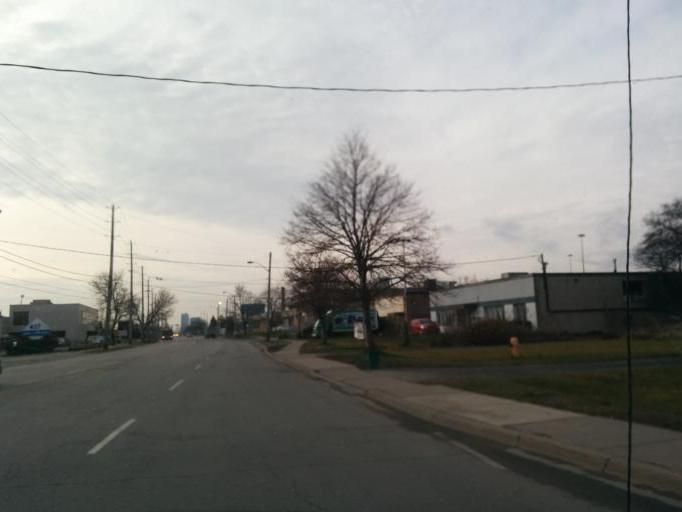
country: CA
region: Ontario
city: Etobicoke
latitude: 43.6158
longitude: -79.5260
